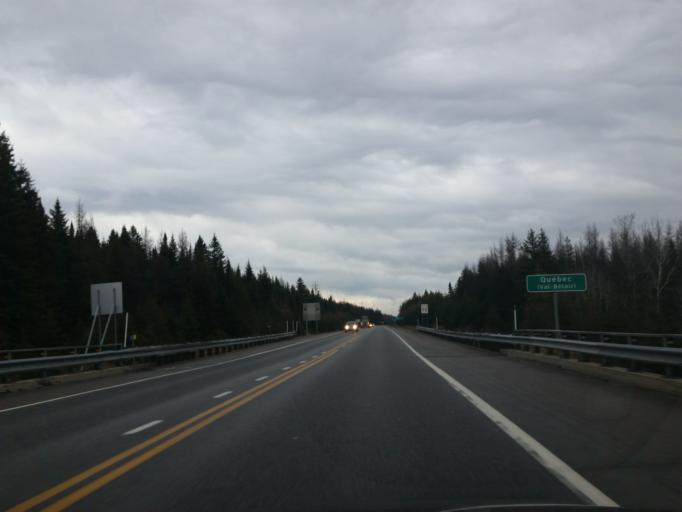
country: CA
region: Quebec
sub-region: Capitale-Nationale
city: Shannon
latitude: 46.8800
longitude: -71.4653
